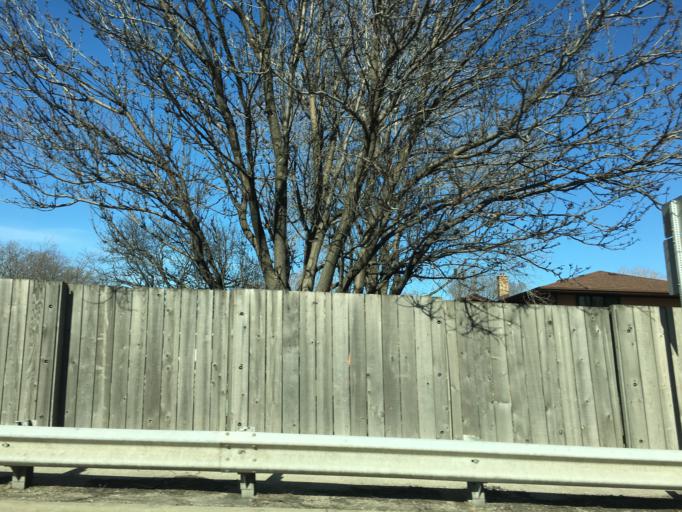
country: US
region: Illinois
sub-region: Cook County
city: Rolling Meadows
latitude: 42.0615
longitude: -88.0224
